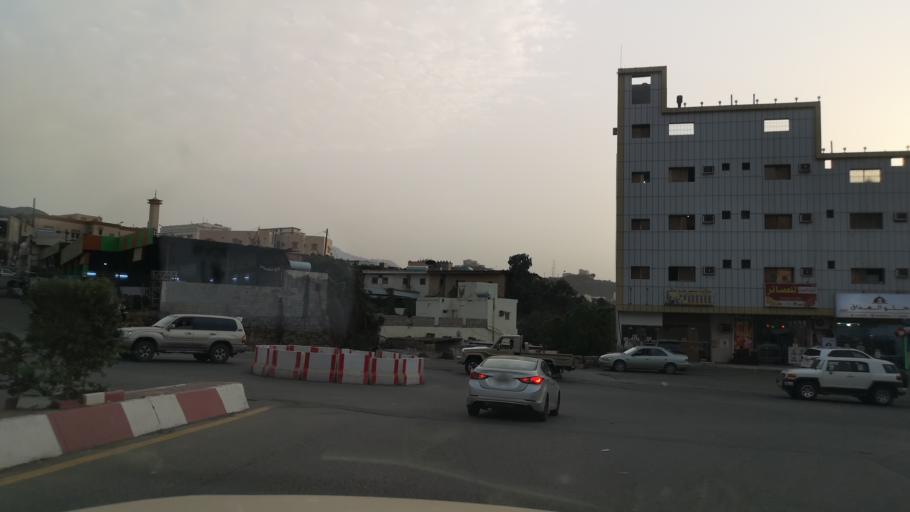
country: YE
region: Sa'dah
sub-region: Monabbih
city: Suq al Khamis
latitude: 17.3385
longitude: 43.1378
